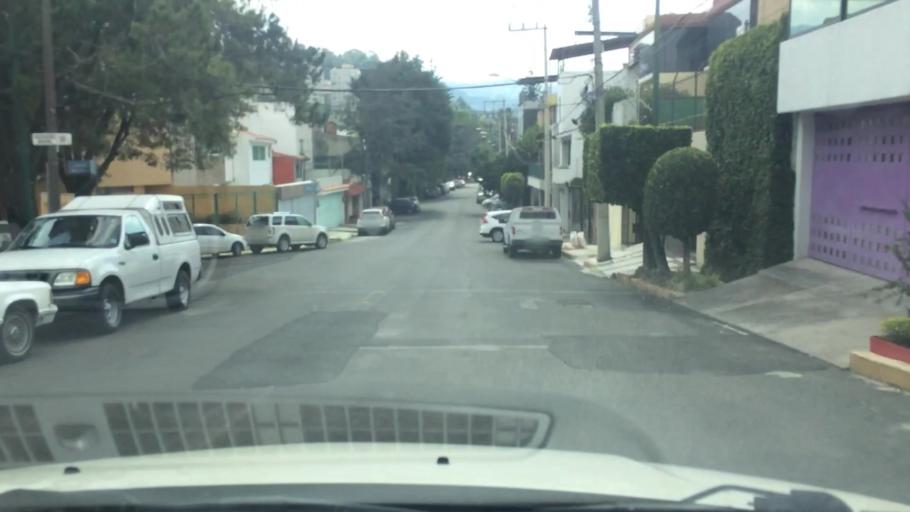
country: MX
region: Mexico City
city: Magdalena Contreras
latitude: 19.3419
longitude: -99.2430
